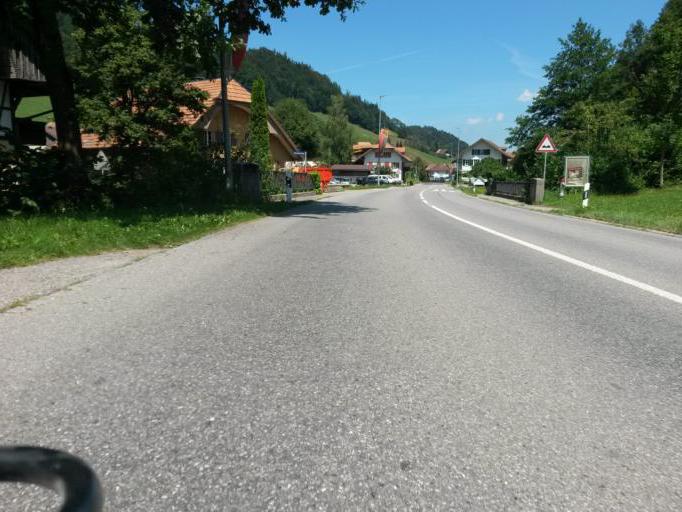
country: CH
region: Bern
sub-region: Bern-Mittelland District
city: Walkringen
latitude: 46.9644
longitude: 7.6232
